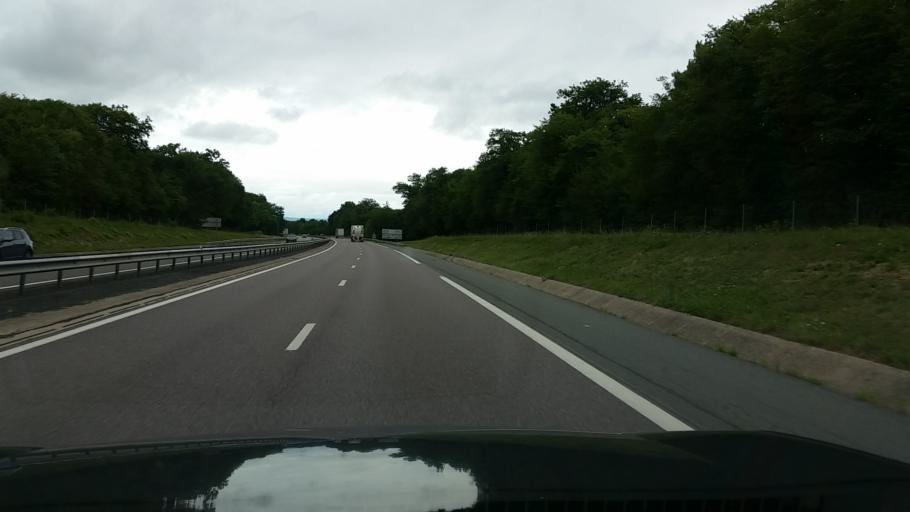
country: FR
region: Lorraine
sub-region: Departement de Meurthe-et-Moselle
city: Colombey-les-Belles
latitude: 48.5247
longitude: 5.9150
